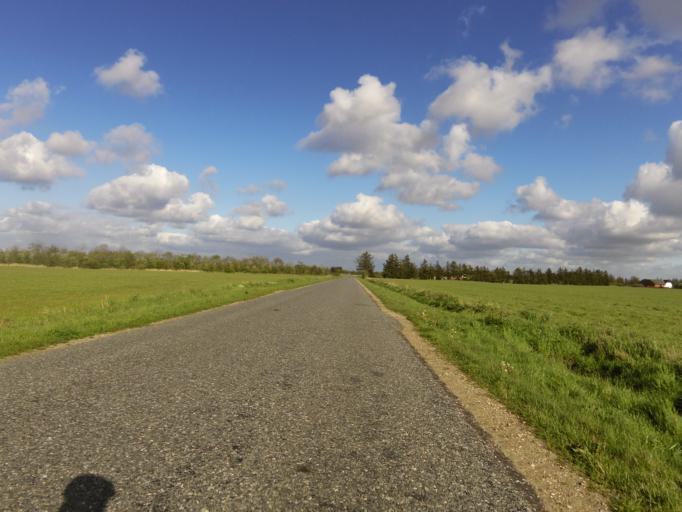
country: DK
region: South Denmark
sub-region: Esbjerg Kommune
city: Ribe
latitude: 55.2596
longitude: 8.7829
